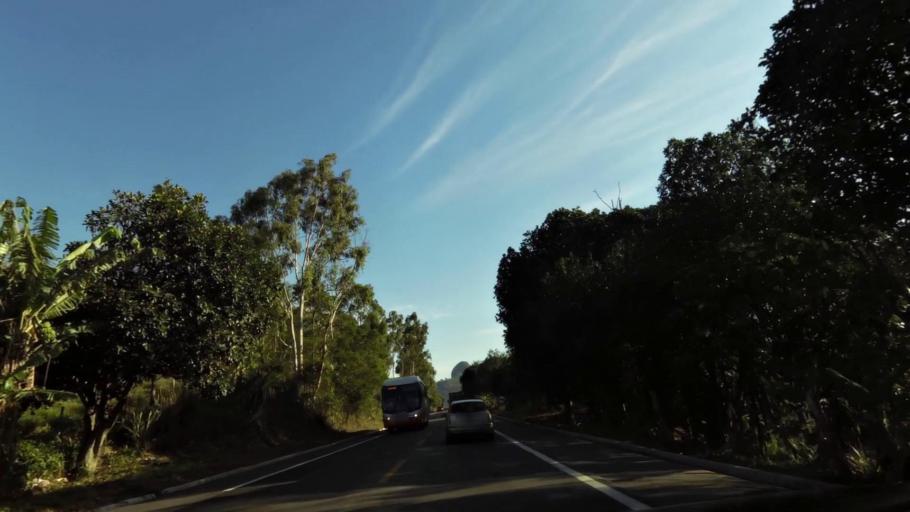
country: BR
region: Espirito Santo
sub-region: Guarapari
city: Guarapari
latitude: -20.5423
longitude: -40.4819
